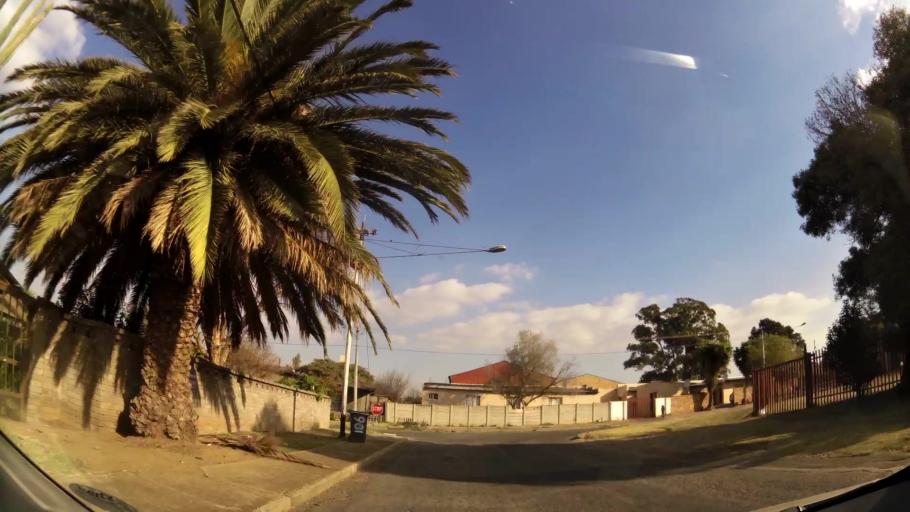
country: ZA
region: Gauteng
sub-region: West Rand District Municipality
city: Krugersdorp
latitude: -26.0999
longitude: 27.7424
